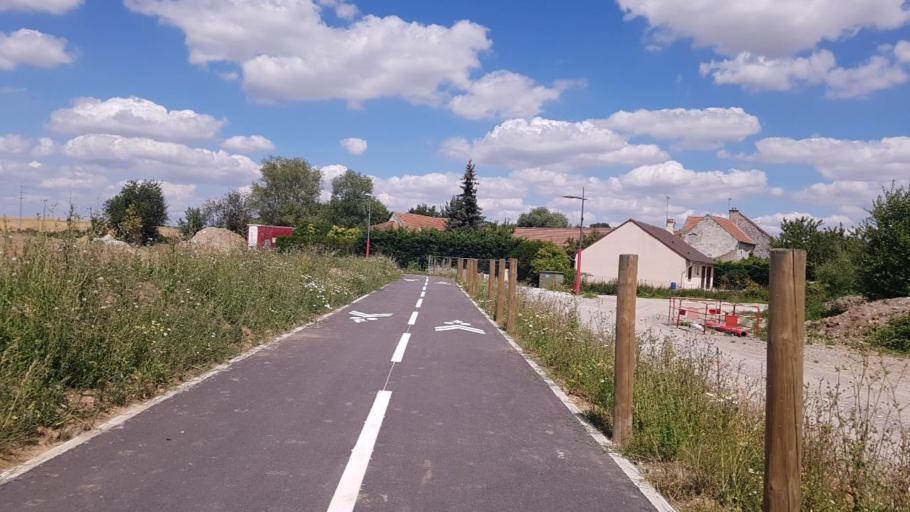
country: FR
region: Ile-de-France
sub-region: Departement de Seine-et-Marne
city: Claye-Souilly
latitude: 48.9808
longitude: 2.6715
